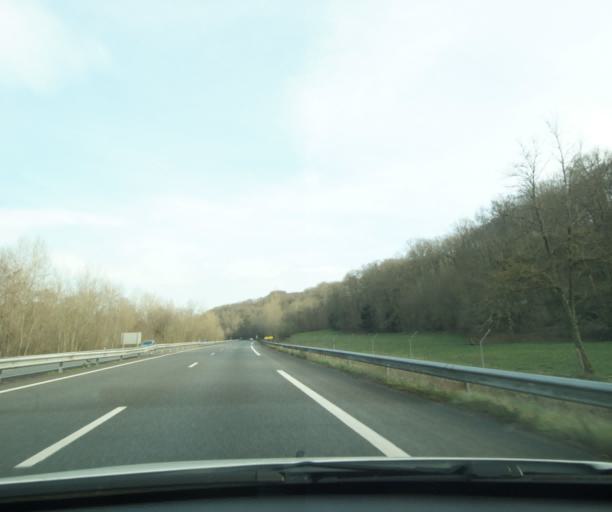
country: FR
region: Midi-Pyrenees
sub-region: Departement des Hautes-Pyrenees
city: Tournay
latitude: 43.1632
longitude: 0.2701
